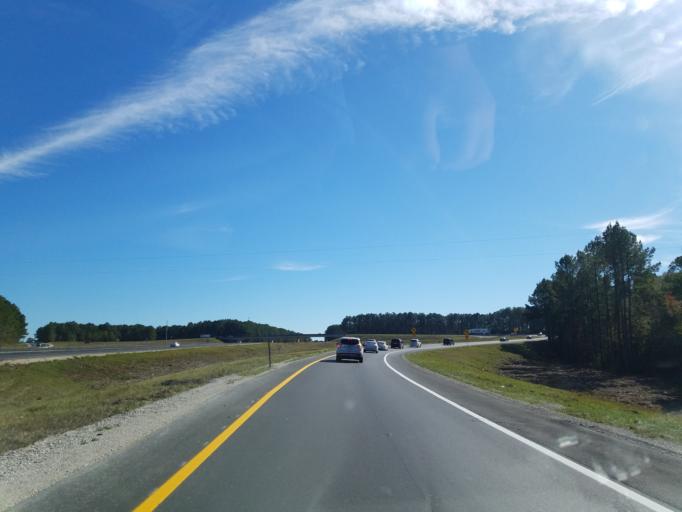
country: US
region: Mississippi
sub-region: Lamar County
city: West Hattiesburg
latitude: 31.2440
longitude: -89.3265
